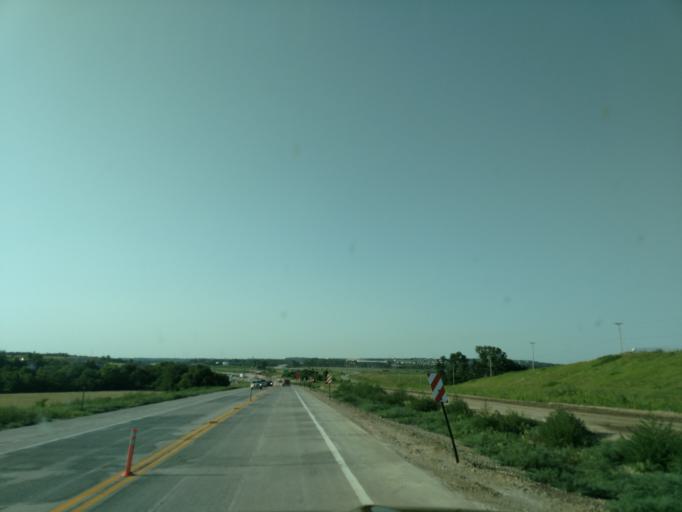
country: US
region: Nebraska
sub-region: Sarpy County
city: Offutt Air Force Base
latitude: 41.0932
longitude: -95.9281
